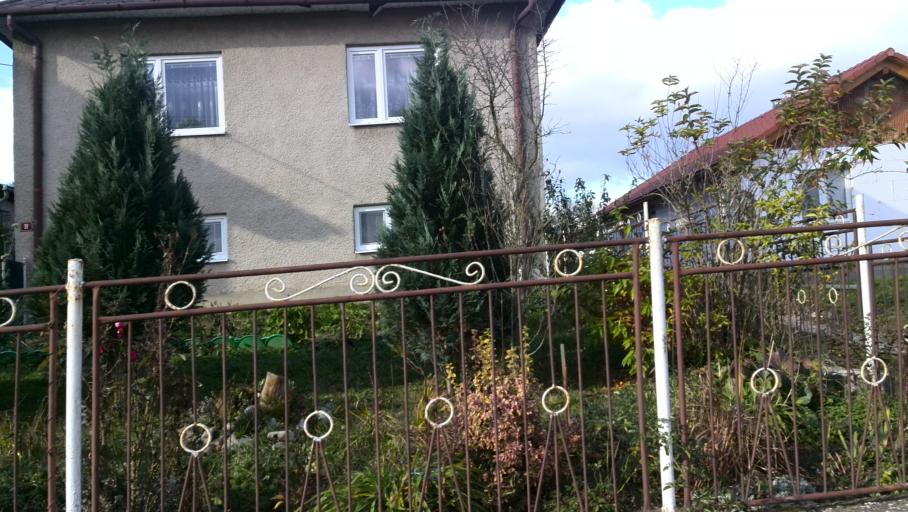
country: SK
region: Presovsky
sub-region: Okres Presov
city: Presov
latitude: 48.9385
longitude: 21.1766
